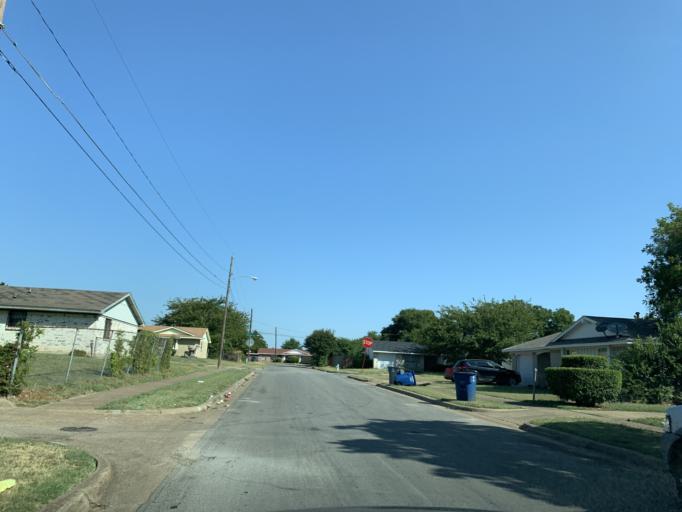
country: US
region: Texas
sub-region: Dallas County
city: Hutchins
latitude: 32.6646
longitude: -96.7614
